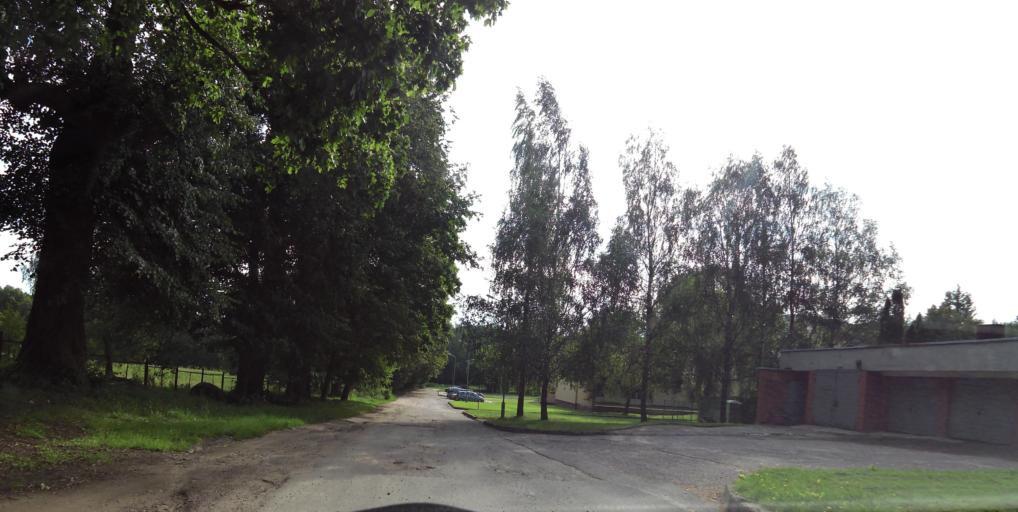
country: LT
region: Vilnius County
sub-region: Vilnius
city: Fabijoniskes
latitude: 54.7393
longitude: 25.2807
